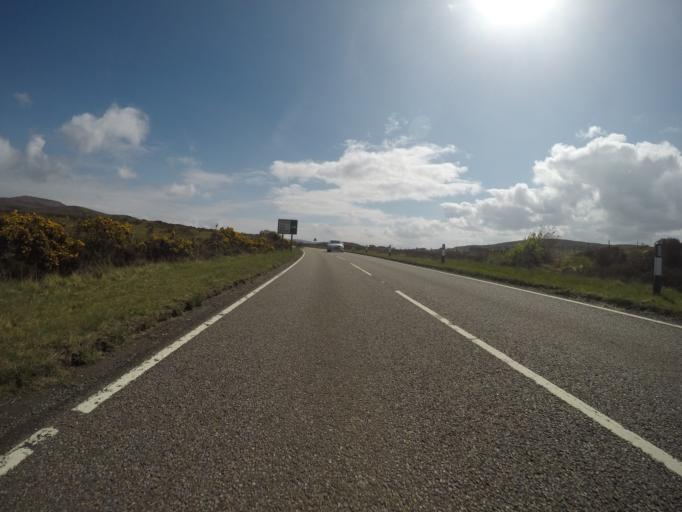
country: GB
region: Scotland
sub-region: Highland
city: Portree
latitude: 57.4754
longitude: -6.2995
